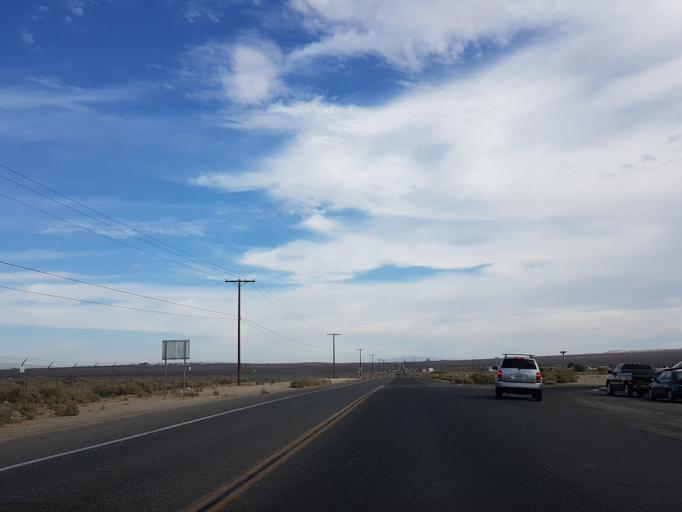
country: US
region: California
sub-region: Kern County
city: Ridgecrest
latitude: 35.6225
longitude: -117.6440
